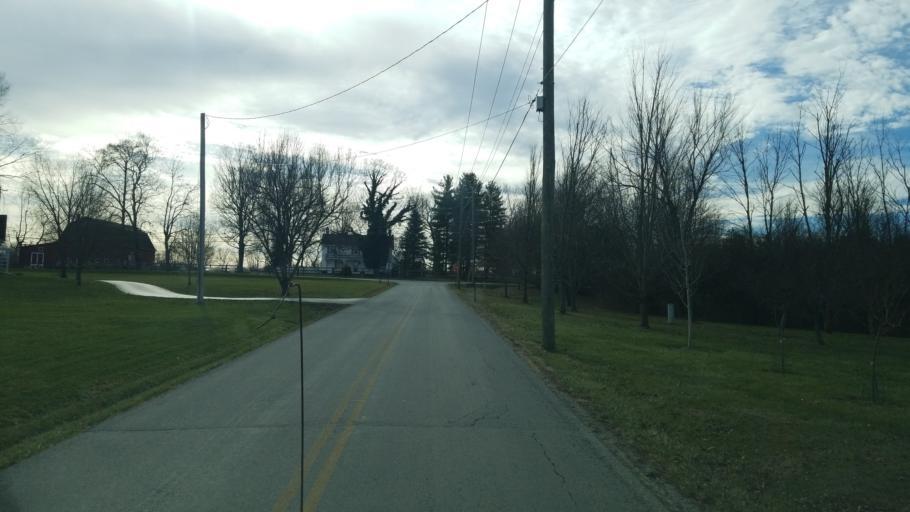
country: US
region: Ohio
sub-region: Warren County
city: Lebanon
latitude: 39.4196
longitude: -84.1604
